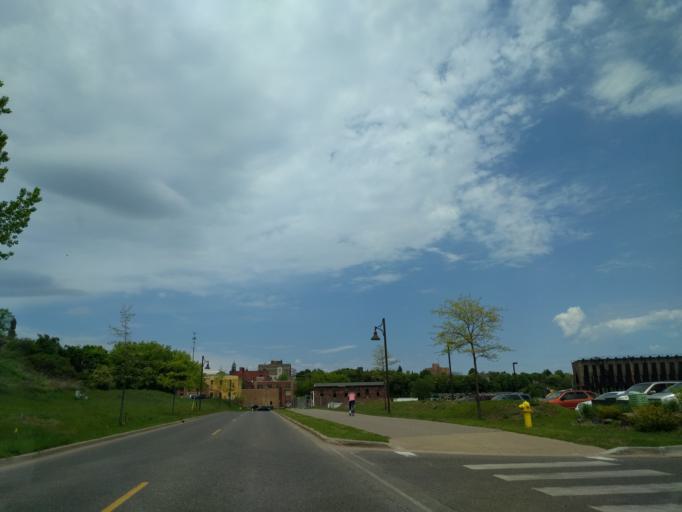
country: US
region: Michigan
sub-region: Marquette County
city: Marquette
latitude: 46.5390
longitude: -87.3931
